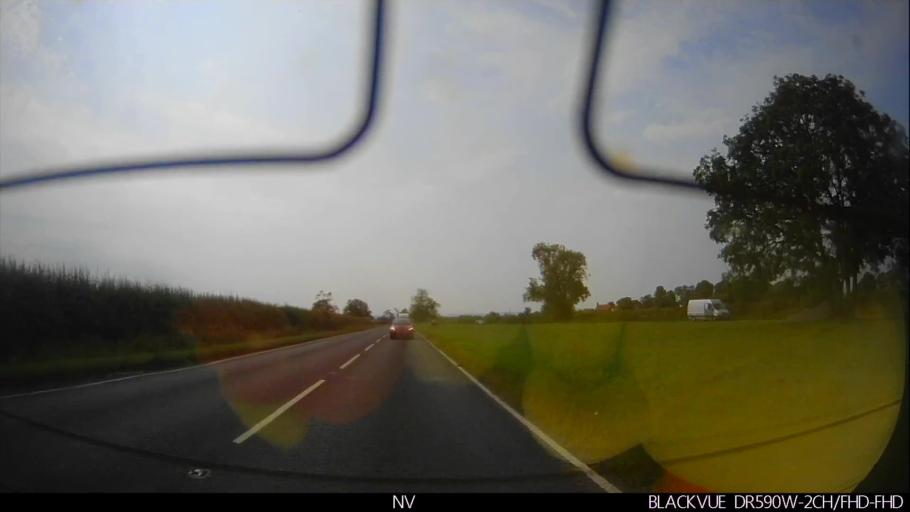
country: GB
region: England
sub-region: North Yorkshire
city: Marishes
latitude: 54.1801
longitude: -0.7611
